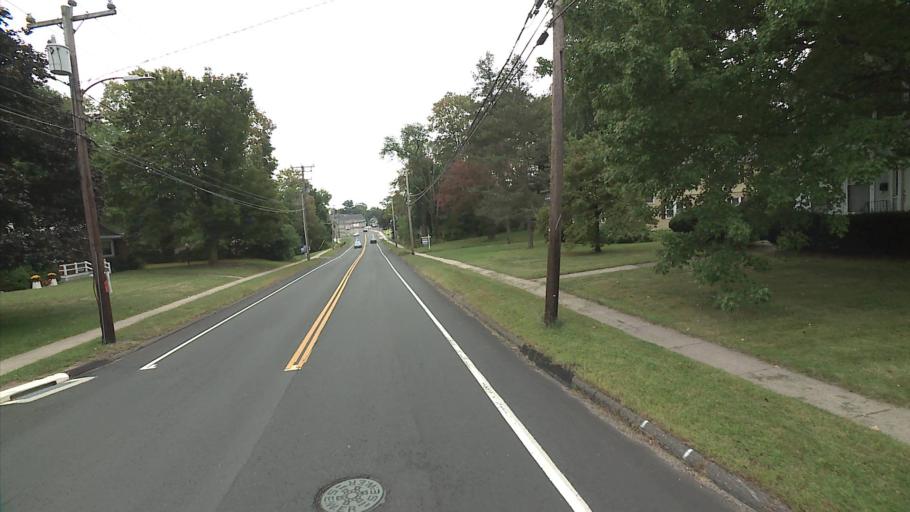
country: US
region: Connecticut
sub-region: Hartford County
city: Windsor
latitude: 41.8578
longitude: -72.6508
